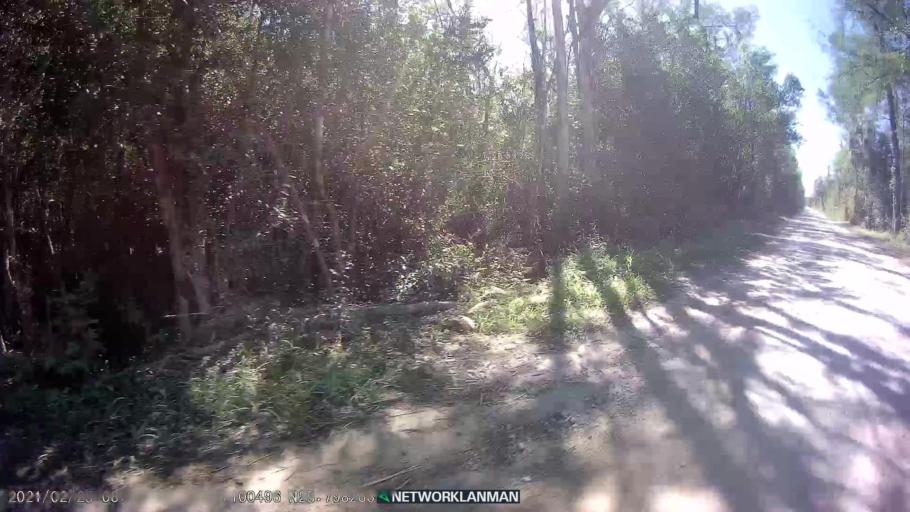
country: US
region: Florida
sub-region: Collier County
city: Marco
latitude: 25.7982
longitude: -81.1005
